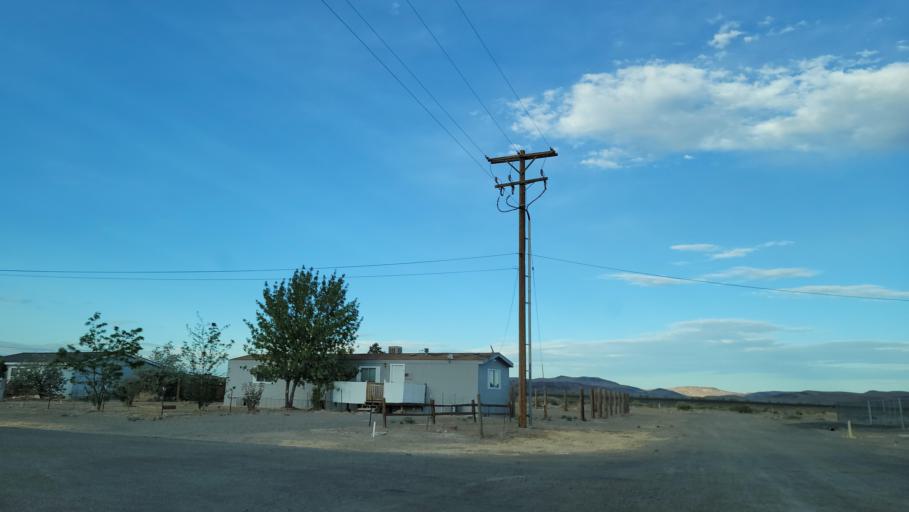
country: US
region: Nevada
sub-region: Lyon County
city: Silver Springs
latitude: 39.4045
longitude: -119.2149
